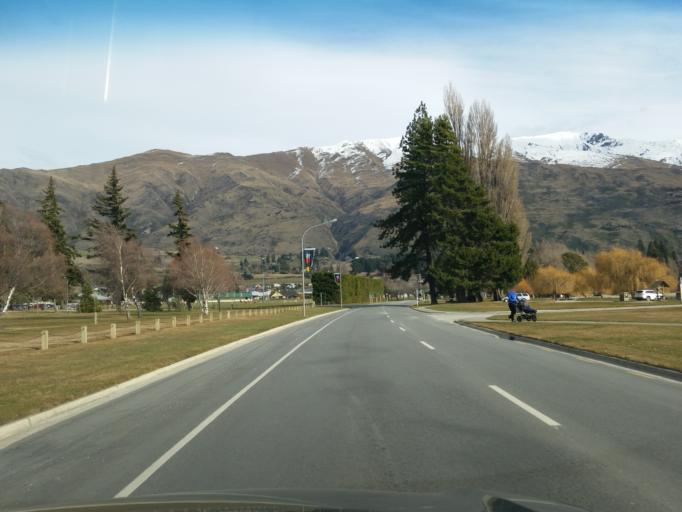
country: NZ
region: Otago
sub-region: Queenstown-Lakes District
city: Wanaka
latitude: -44.6981
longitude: 169.1291
